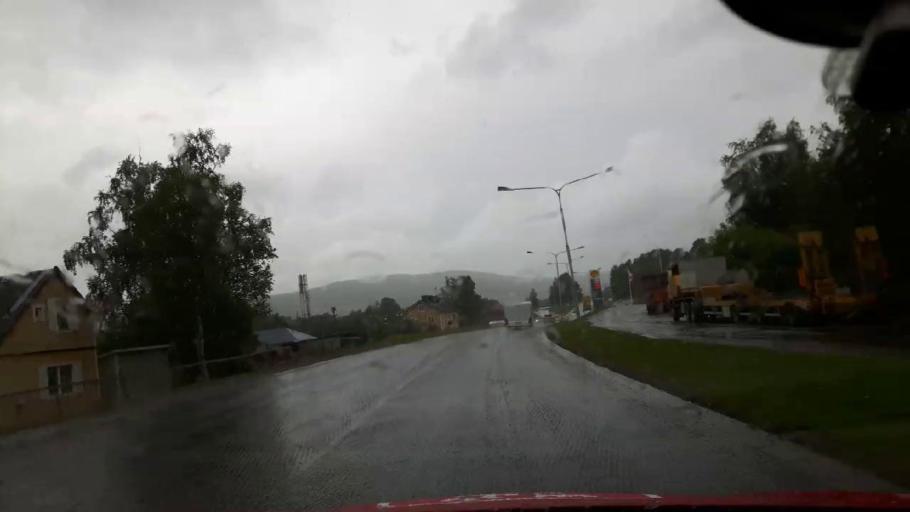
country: SE
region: Jaemtland
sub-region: Are Kommun
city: Jarpen
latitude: 63.3419
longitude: 13.4756
